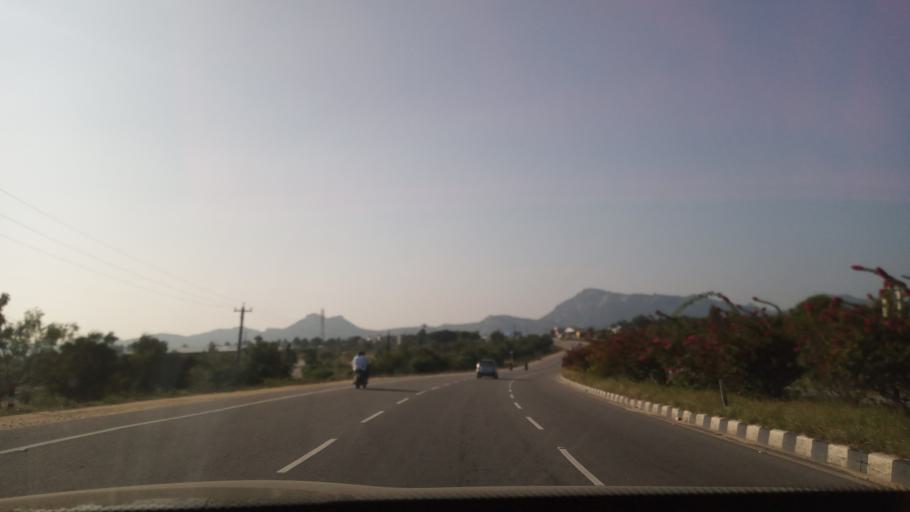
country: IN
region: Tamil Nadu
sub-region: Krishnagiri
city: Krishnagiri
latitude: 12.5846
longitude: 78.1501
